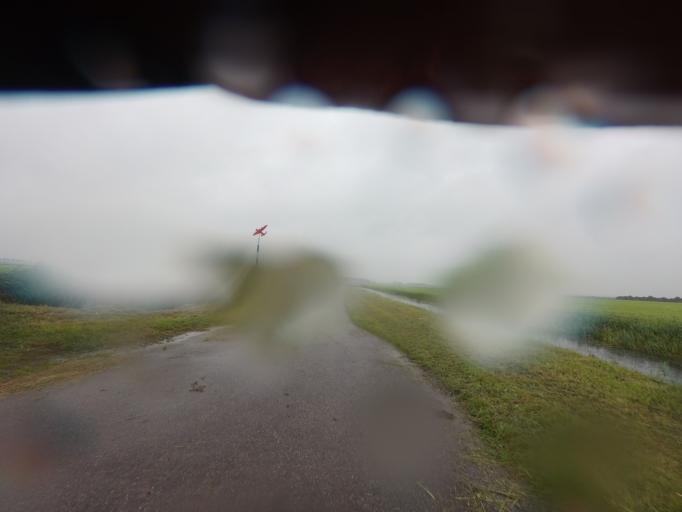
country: NL
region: North Holland
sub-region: Gemeente Medemblik
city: Opperdoes
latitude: 52.7404
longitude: 5.0474
